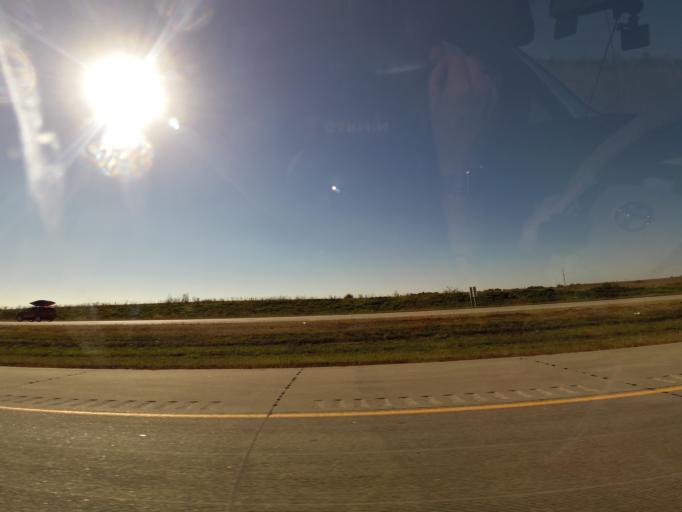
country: US
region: Nebraska
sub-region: Lancaster County
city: Waverly
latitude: 40.9088
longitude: -96.4958
